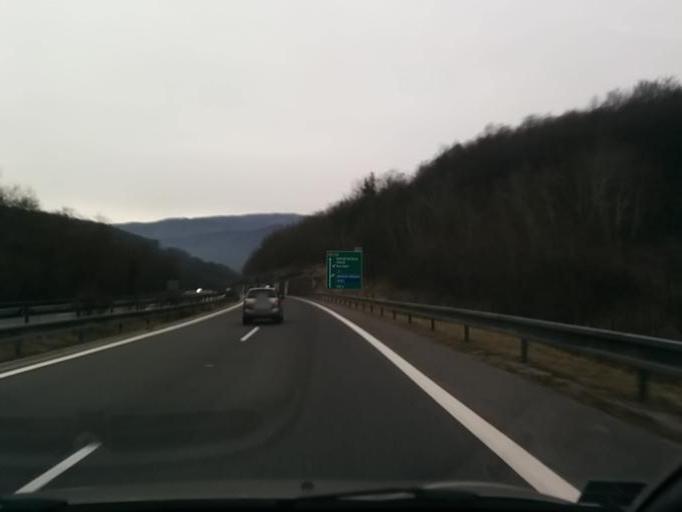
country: SK
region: Nitriansky
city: Tlmace
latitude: 48.3636
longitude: 18.5631
